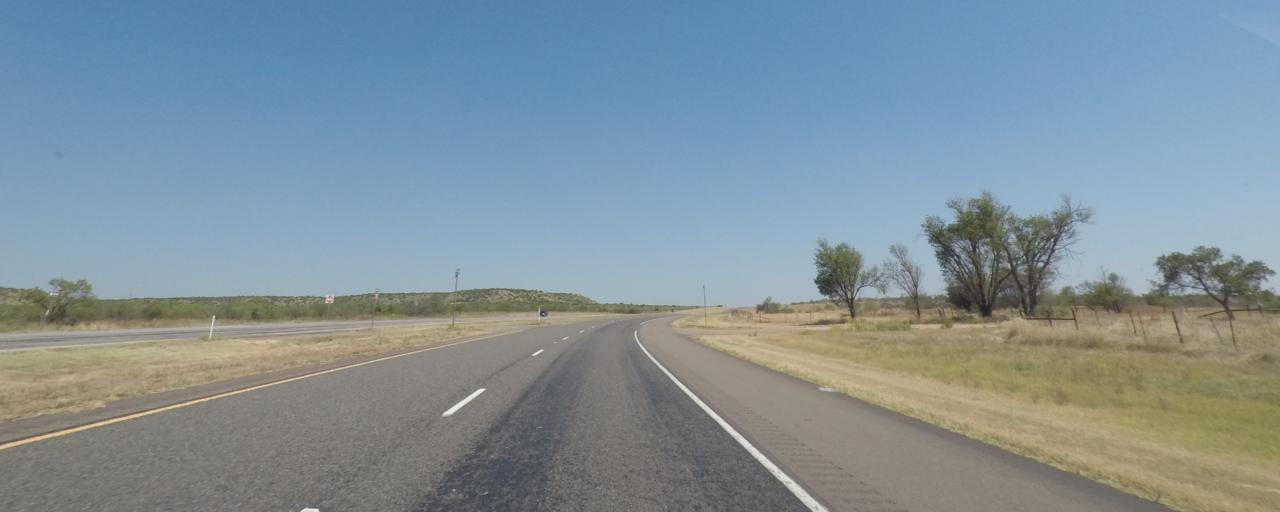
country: US
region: Texas
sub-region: Dickens County
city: Dickens
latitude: 33.6328
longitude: -100.8801
